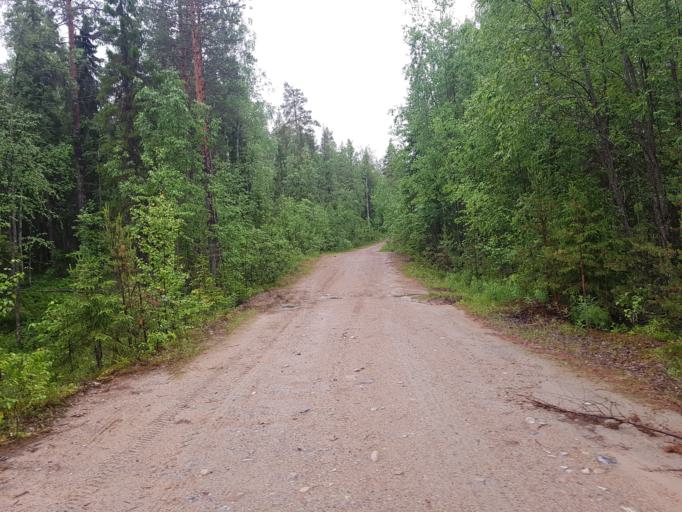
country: RU
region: Republic of Karelia
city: Kostomuksha
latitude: 64.8791
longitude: 30.2622
